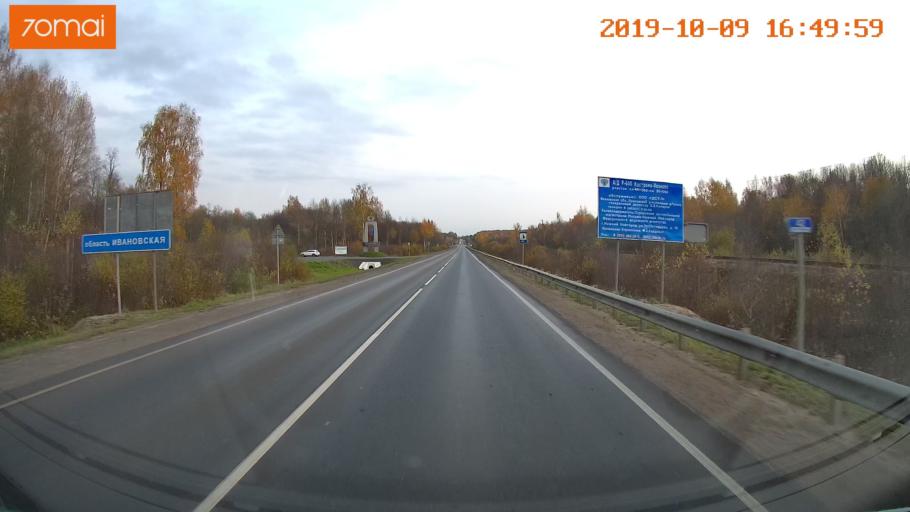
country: RU
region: Kostroma
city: Volgorechensk
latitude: 57.4072
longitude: 41.2030
